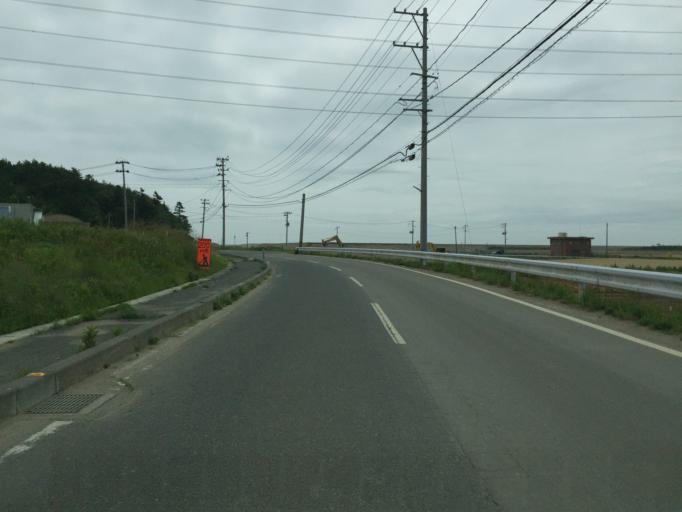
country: JP
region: Fukushima
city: Namie
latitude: 37.6626
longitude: 141.0135
